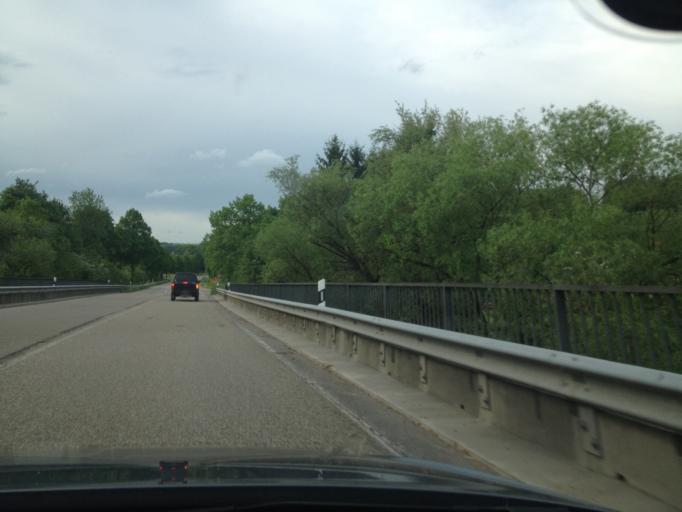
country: DE
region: Rheinland-Pfalz
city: Dellfeld
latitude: 49.2281
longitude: 7.4643
